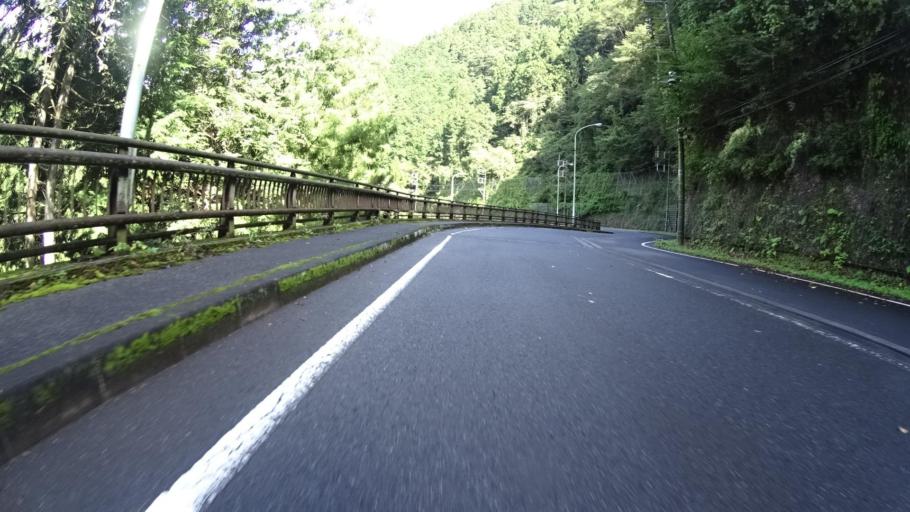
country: JP
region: Yamanashi
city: Uenohara
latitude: 35.7363
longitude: 139.0920
